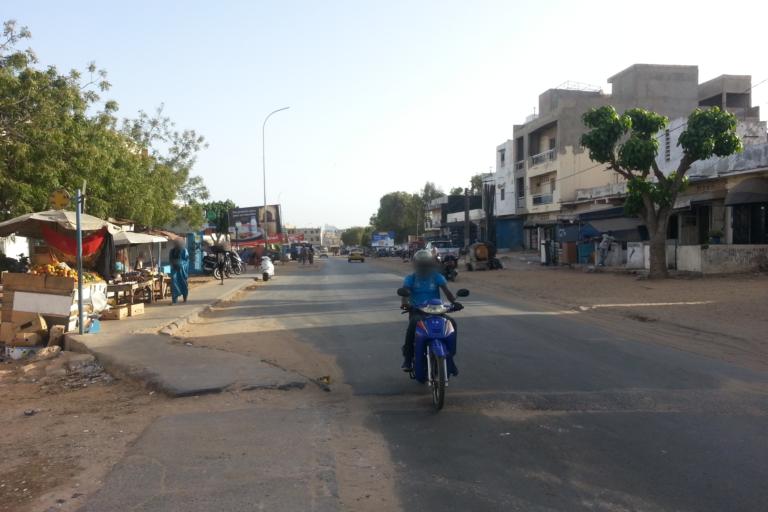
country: SN
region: Dakar
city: Pikine
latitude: 14.7730
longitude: -17.3843
